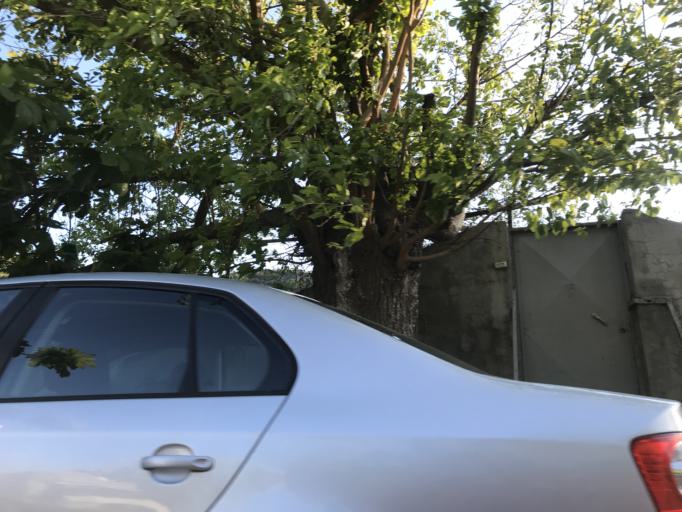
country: TR
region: Hatay
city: Buyukcat
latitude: 36.0759
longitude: 36.0427
